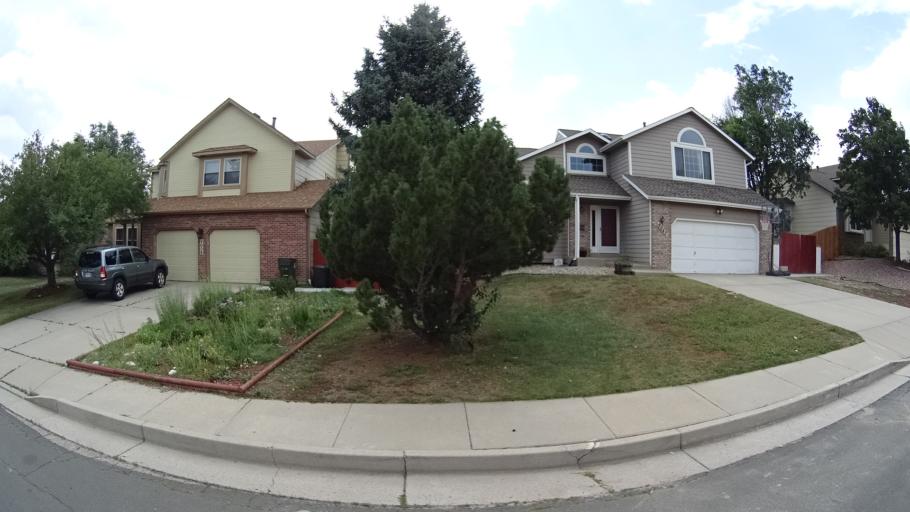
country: US
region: Colorado
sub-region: El Paso County
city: Black Forest
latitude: 38.9586
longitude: -104.7408
